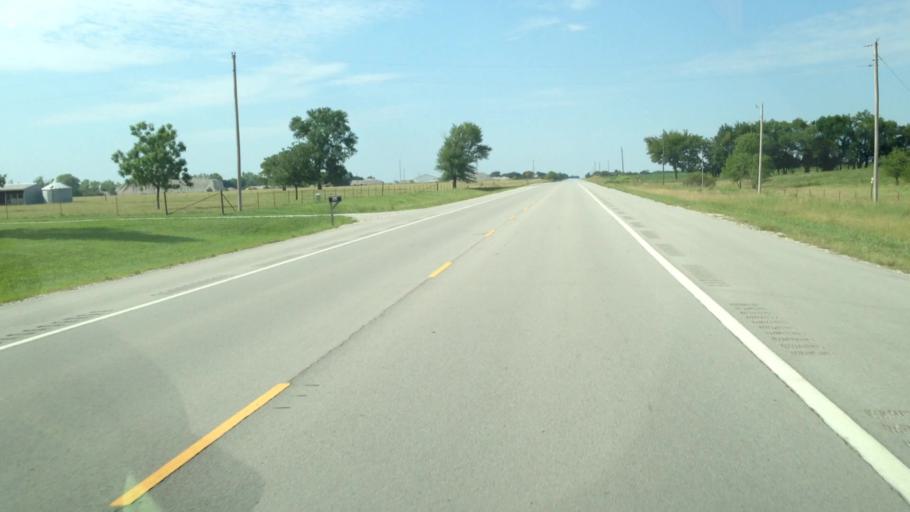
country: US
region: Kansas
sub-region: Labette County
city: Parsons
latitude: 37.2755
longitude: -95.2674
